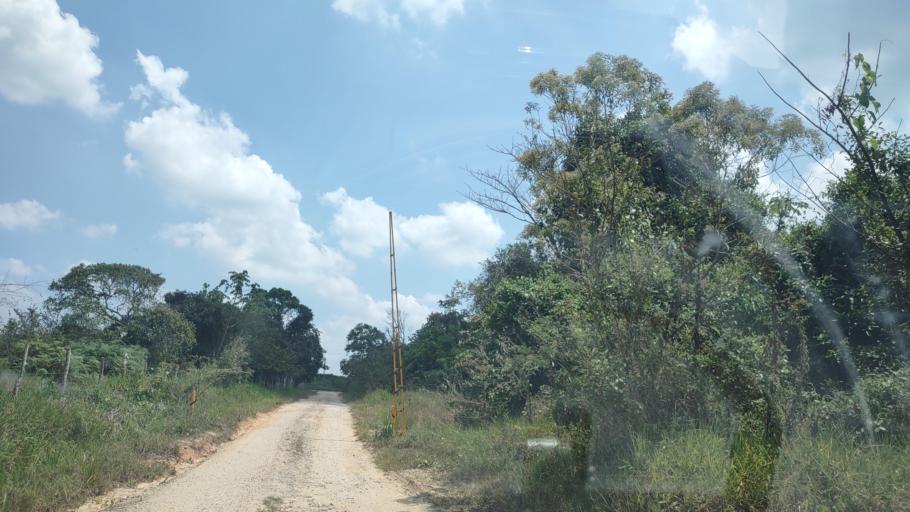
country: MX
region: Veracruz
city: Las Choapas
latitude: 17.9263
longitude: -94.1450
